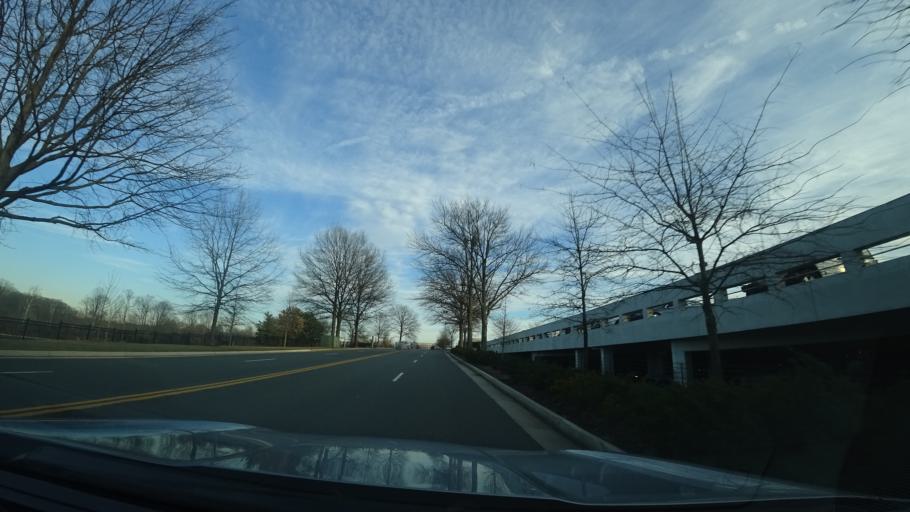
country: US
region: Virginia
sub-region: Fairfax County
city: Greenbriar
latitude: 38.8654
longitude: -77.3594
